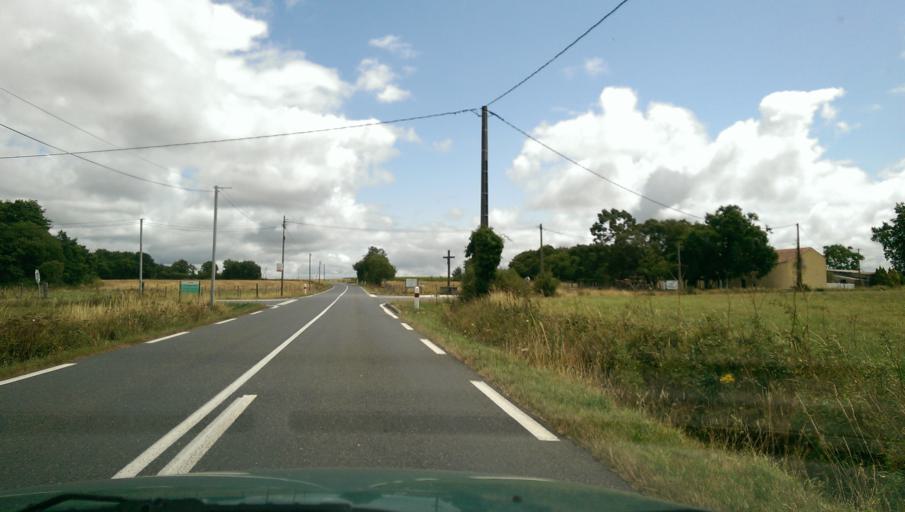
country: FR
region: Pays de la Loire
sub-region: Departement de la Loire-Atlantique
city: Remouille
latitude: 47.0750
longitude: -1.3670
